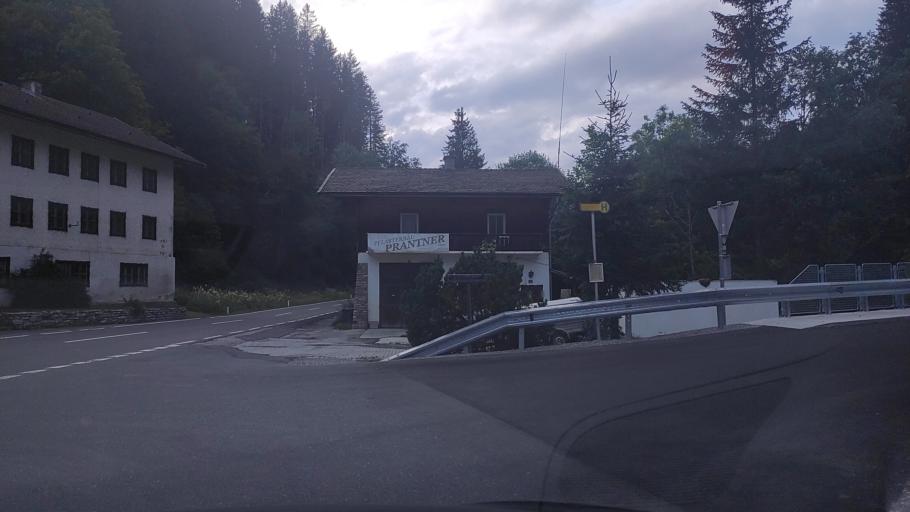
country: AT
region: Salzburg
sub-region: Politischer Bezirk Zell am See
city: Taxenbach
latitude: 47.2672
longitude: 12.9797
